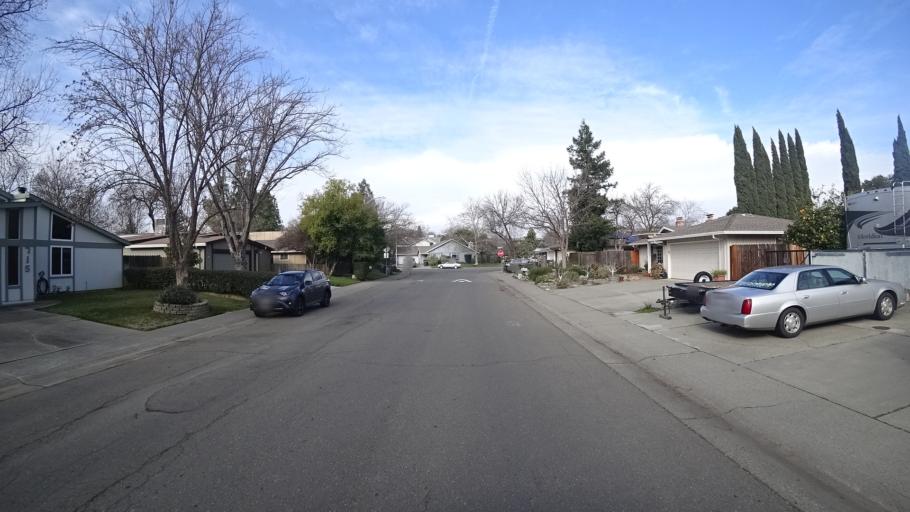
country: US
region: California
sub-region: Yolo County
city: Davis
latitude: 38.5456
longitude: -121.7151
